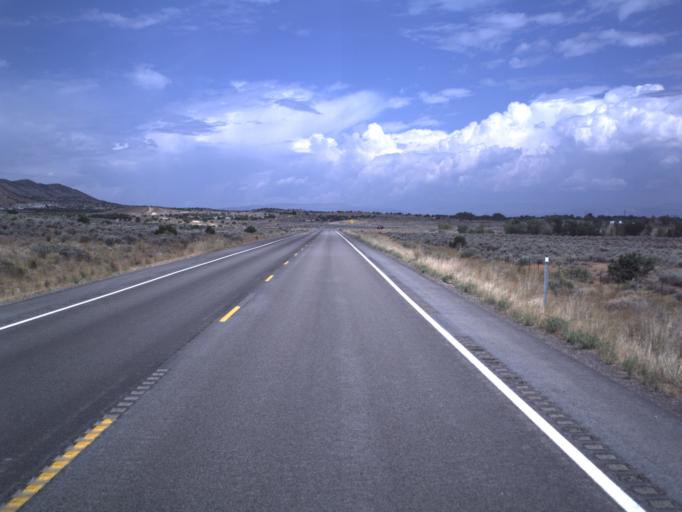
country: US
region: Utah
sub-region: Uintah County
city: Naples
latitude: 40.3519
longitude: -109.4929
